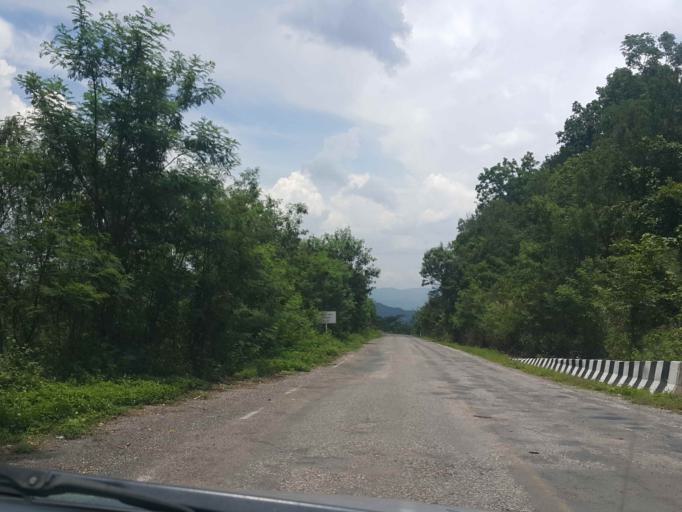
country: TH
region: Phayao
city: Chiang Muan
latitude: 18.9208
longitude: 100.2014
